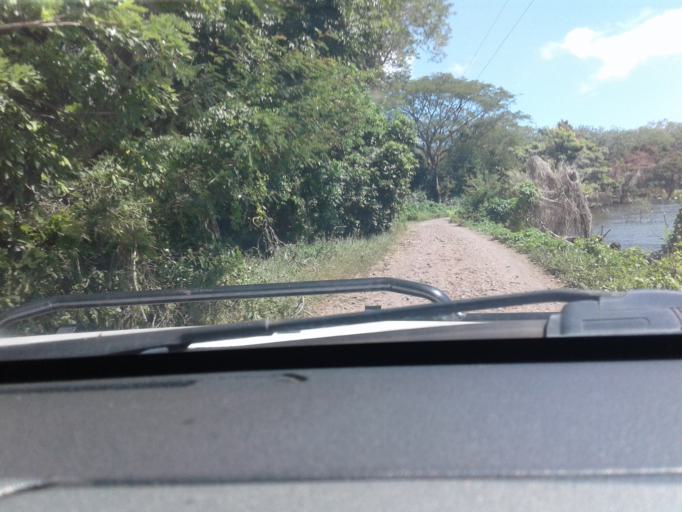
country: NI
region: Rivas
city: Altagracia
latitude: 11.4289
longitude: -85.5517
